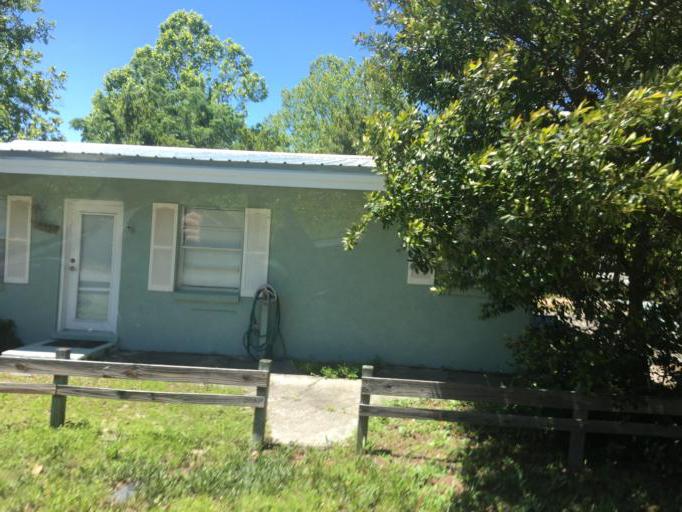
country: US
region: Florida
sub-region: Bay County
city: Laguna Beach
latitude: 30.2462
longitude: -85.9293
